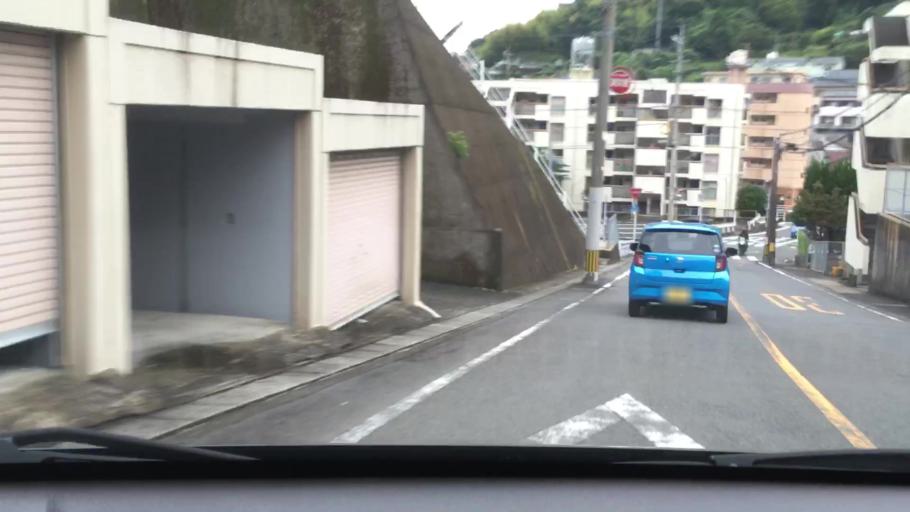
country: JP
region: Nagasaki
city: Nagasaki-shi
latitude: 32.7603
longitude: 129.9365
